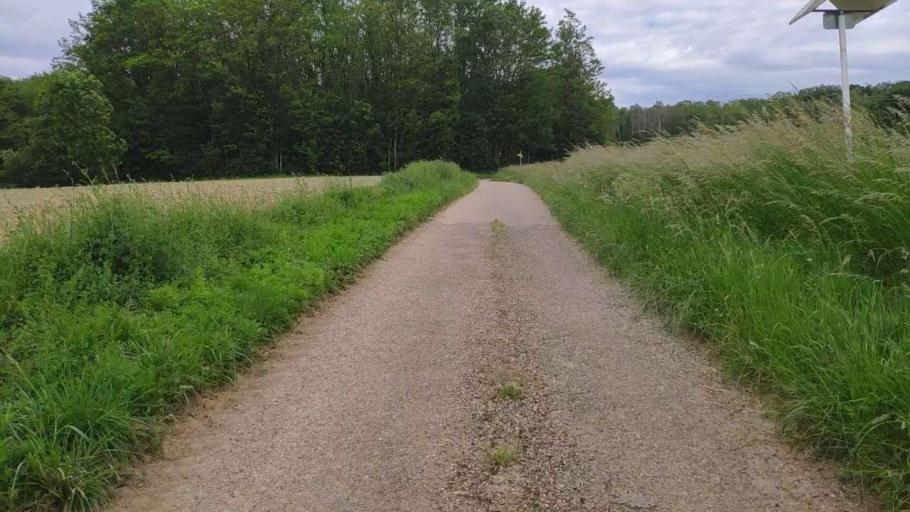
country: FR
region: Franche-Comte
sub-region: Departement du Jura
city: Bletterans
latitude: 46.7877
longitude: 5.5457
